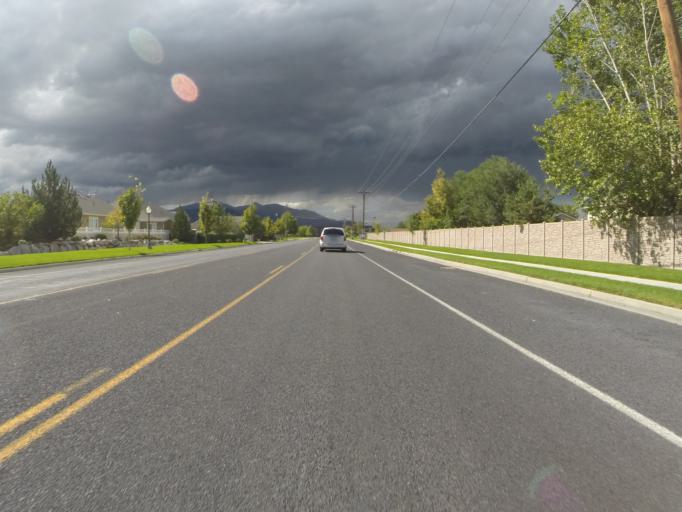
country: US
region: Utah
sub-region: Salt Lake County
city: West Valley City
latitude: 40.7039
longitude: -112.0138
